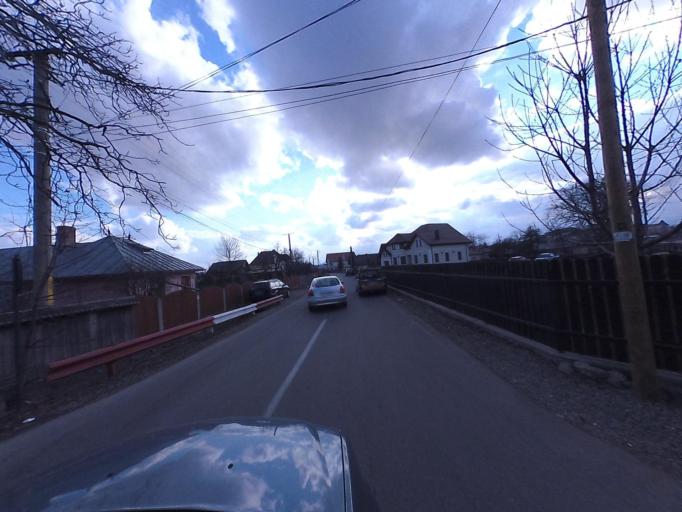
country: RO
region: Neamt
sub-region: Oras Targu Neamt
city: Targu Neamt
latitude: 47.2092
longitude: 26.3742
